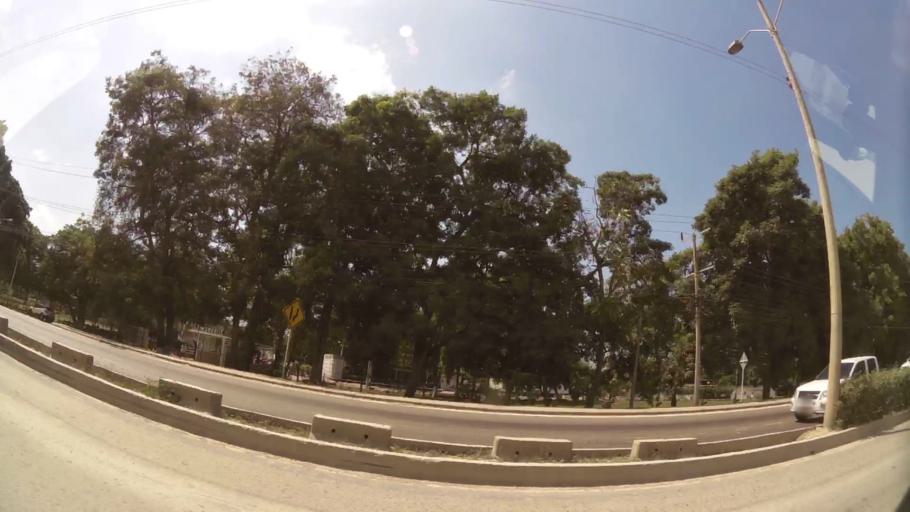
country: CO
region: Bolivar
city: Cartagena
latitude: 10.3610
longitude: -75.5072
